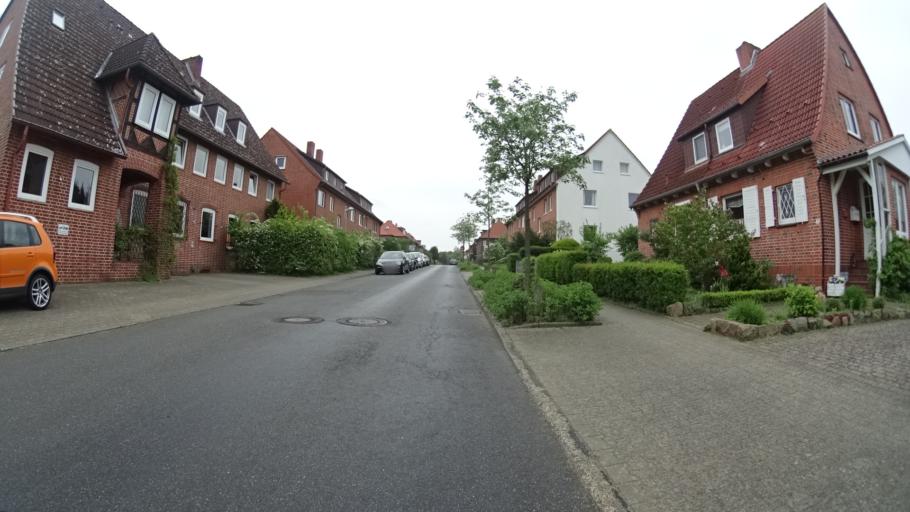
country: DE
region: Lower Saxony
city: Lueneburg
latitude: 53.2414
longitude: 10.3912
